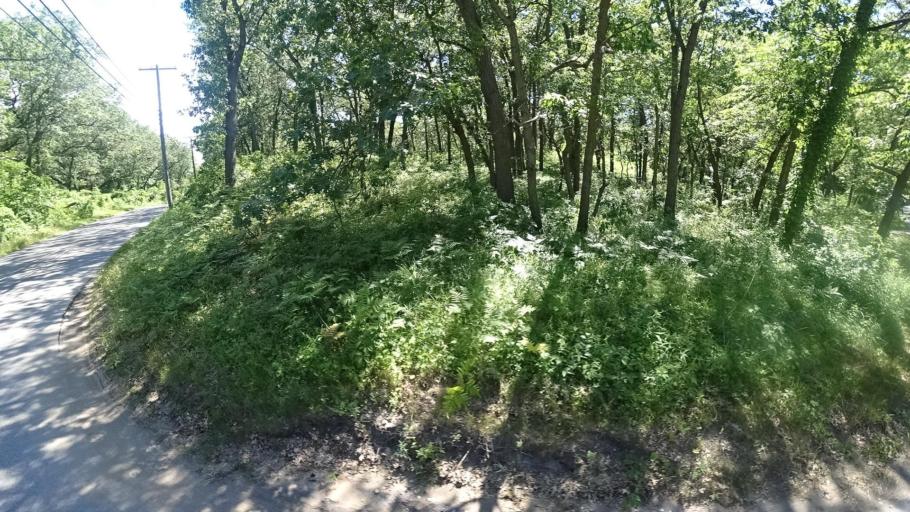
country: US
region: Indiana
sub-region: Porter County
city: Porter
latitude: 41.6549
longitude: -87.0675
